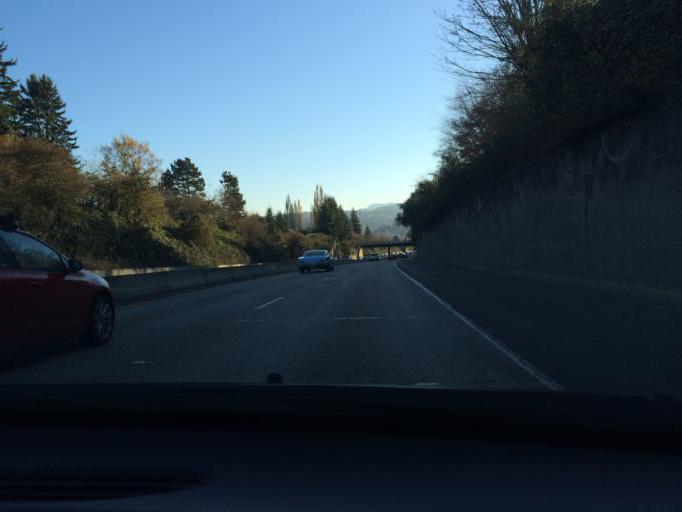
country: US
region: Washington
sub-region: Whatcom County
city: Bellingham
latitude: 48.7681
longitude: -122.4624
